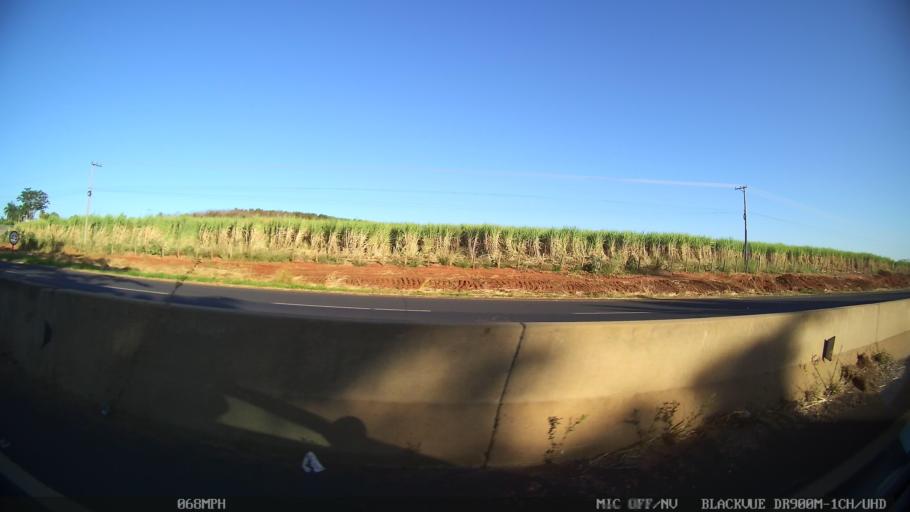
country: BR
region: Sao Paulo
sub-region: Guapiacu
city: Guapiacu
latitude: -20.7868
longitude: -49.2817
